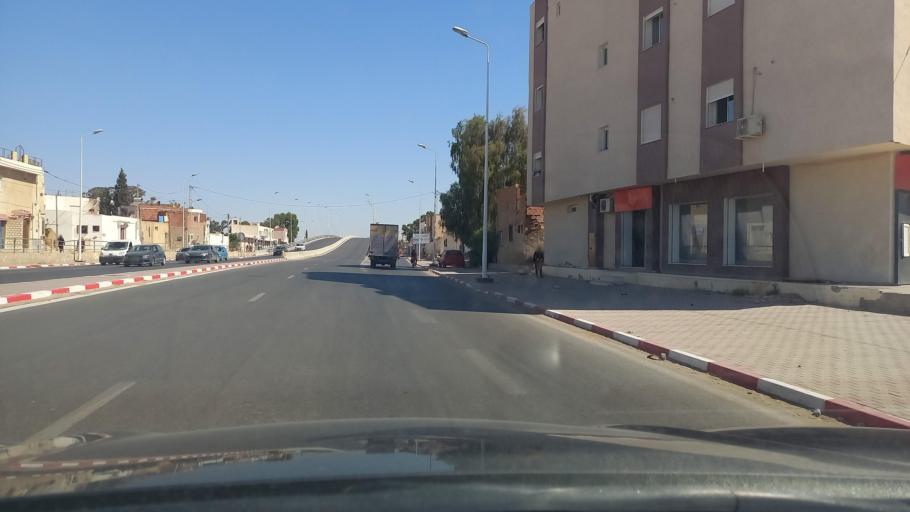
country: TN
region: Safaqis
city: Sfax
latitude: 34.7307
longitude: 10.7252
